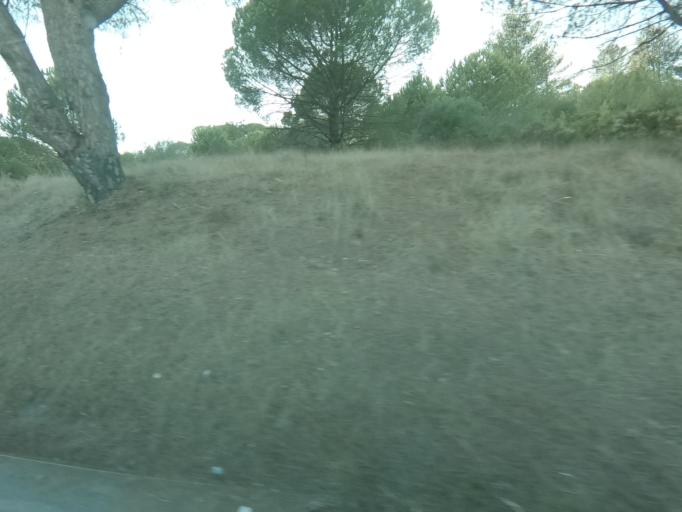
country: PT
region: Setubal
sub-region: Palmela
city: Quinta do Anjo
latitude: 38.5244
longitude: -8.9829
